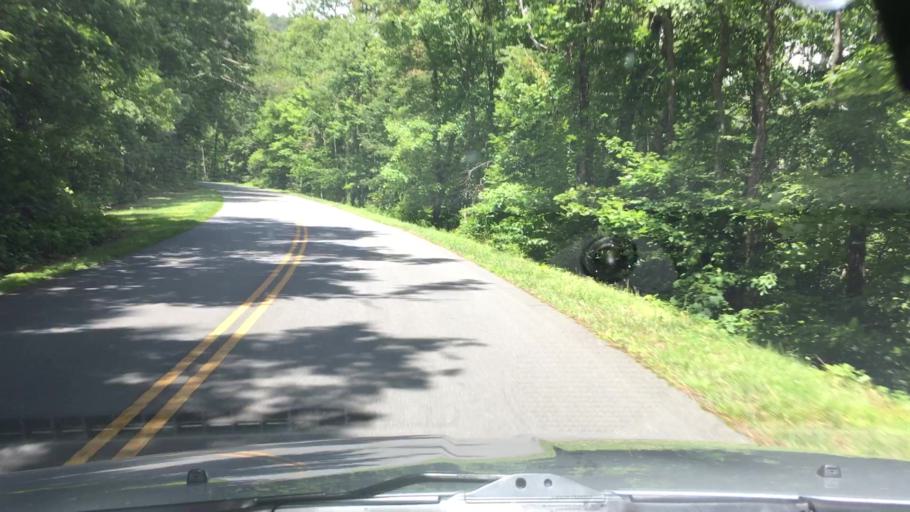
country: US
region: North Carolina
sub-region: Buncombe County
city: Swannanoa
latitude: 35.6578
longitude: -82.4486
